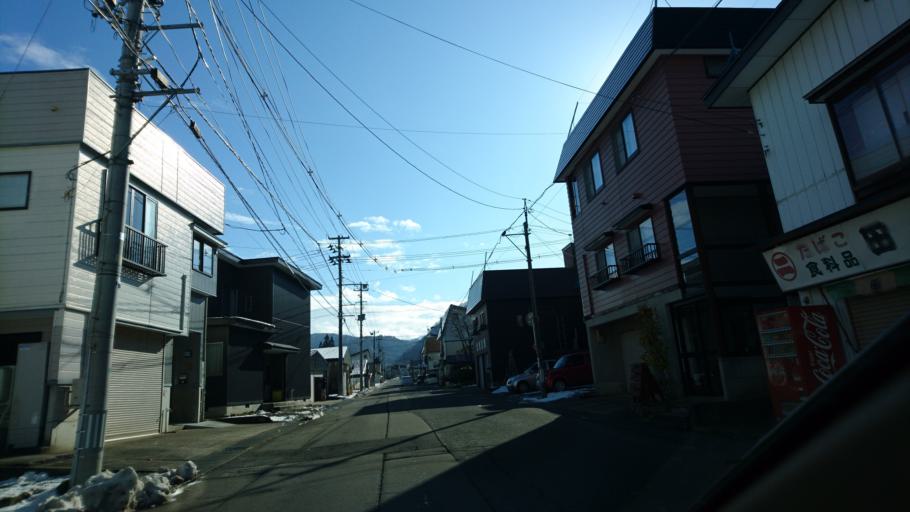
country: JP
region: Akita
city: Yokotemachi
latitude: 39.3129
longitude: 140.7779
